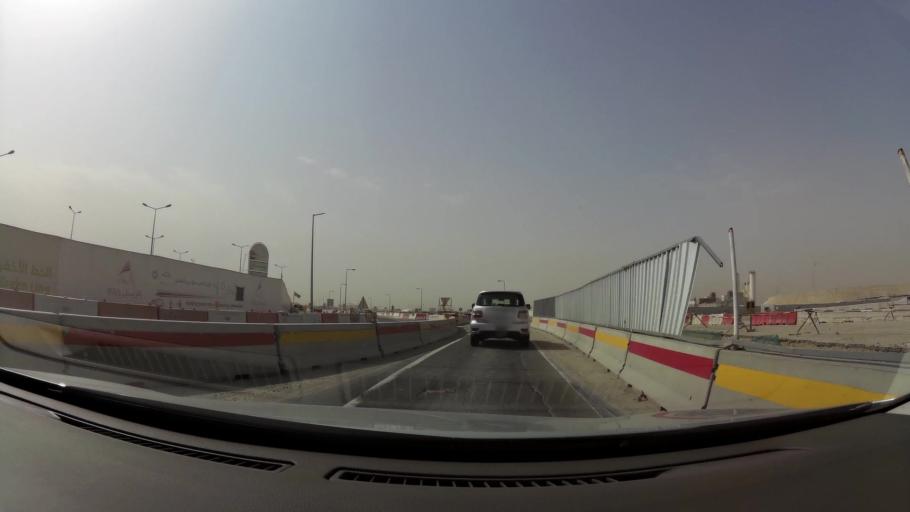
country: QA
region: Baladiyat ad Dawhah
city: Doha
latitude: 25.2924
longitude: 51.4892
